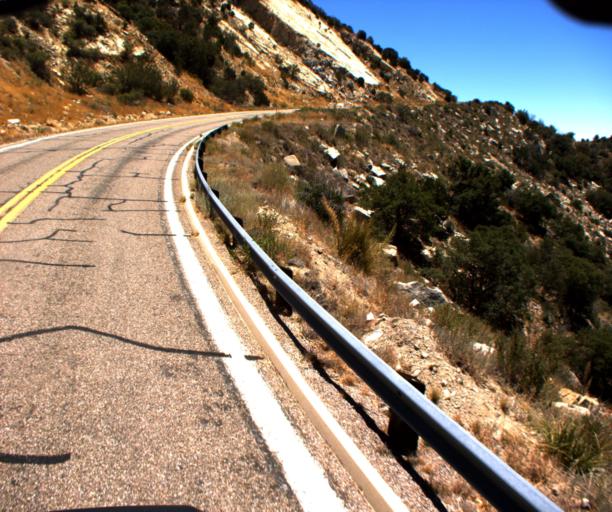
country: US
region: Arizona
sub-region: Pima County
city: Sells
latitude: 31.9580
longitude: -111.6257
